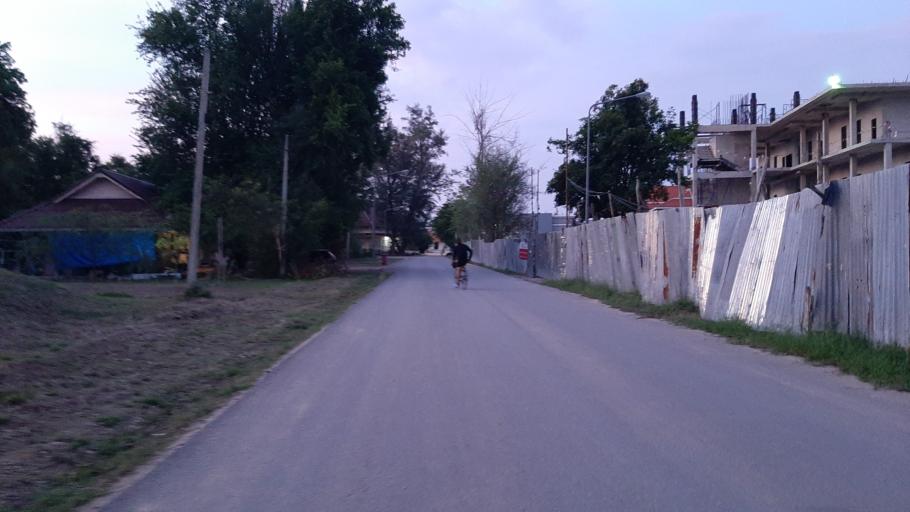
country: TH
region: Phetchaburi
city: Cha-am
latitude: 12.6863
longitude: 99.9618
